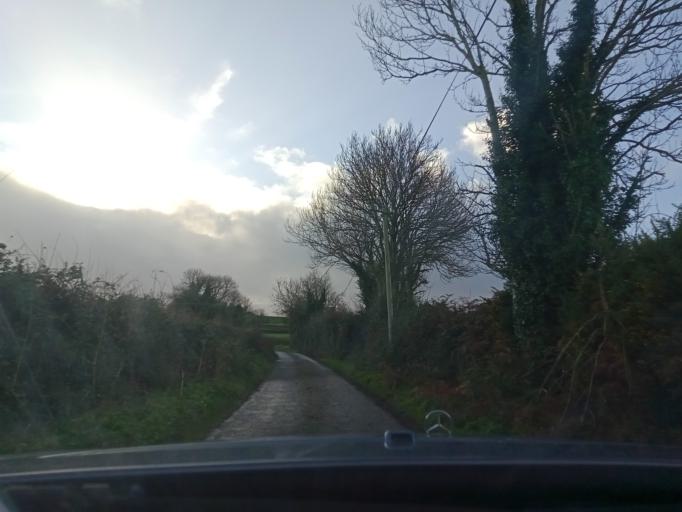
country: IE
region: Leinster
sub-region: Kilkenny
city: Callan
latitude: 52.4676
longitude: -7.3991
